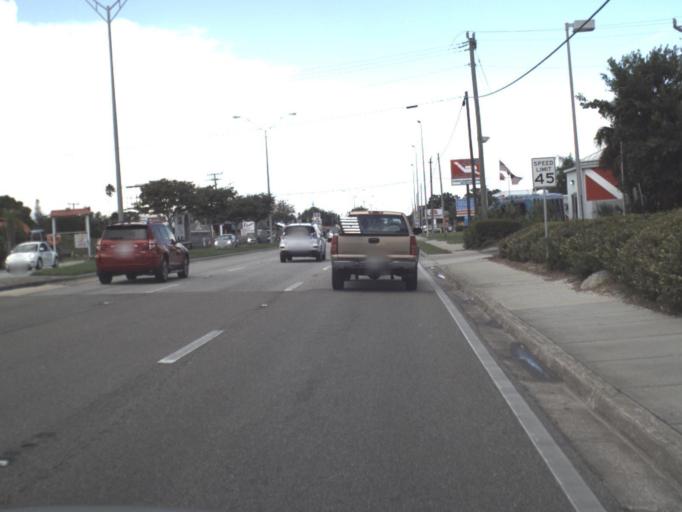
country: US
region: Florida
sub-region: Sarasota County
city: Gulf Gate Estates
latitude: 27.2617
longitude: -82.5236
